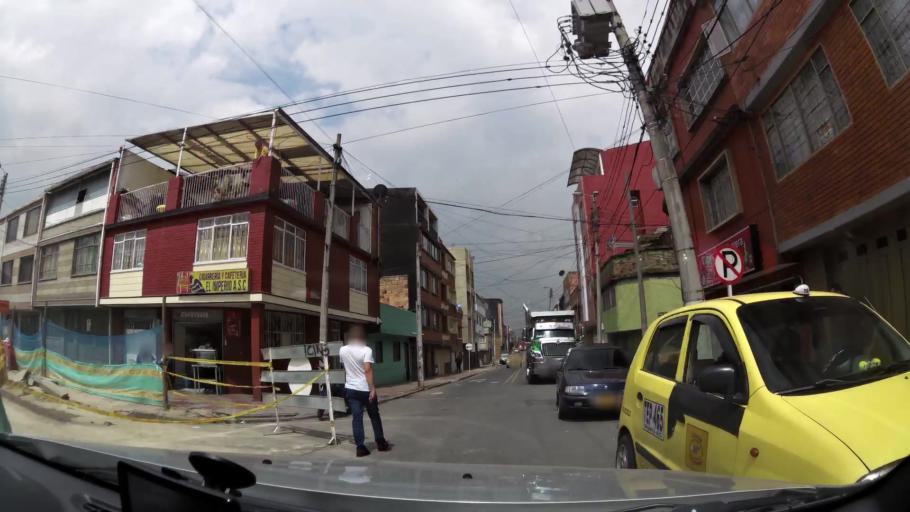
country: CO
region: Bogota D.C.
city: Barrio San Luis
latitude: 4.6821
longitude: -74.0661
